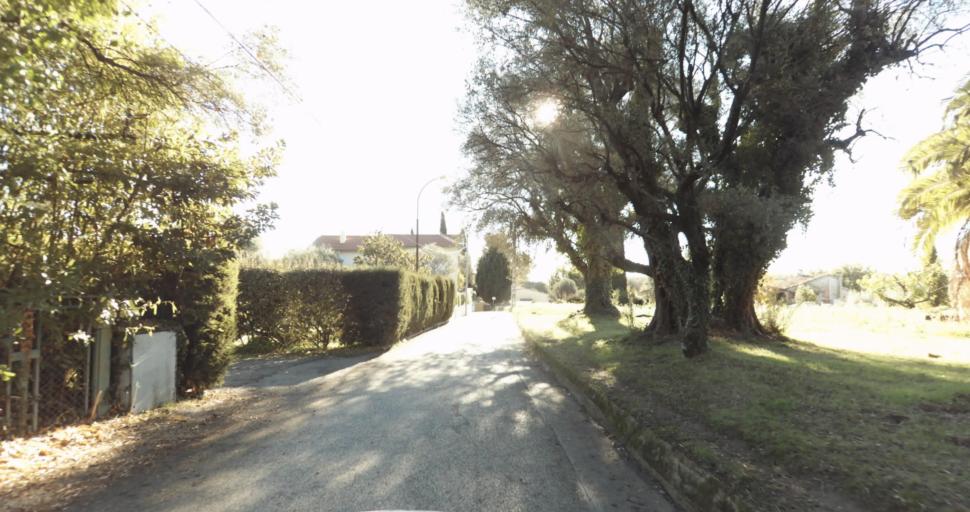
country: FR
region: Provence-Alpes-Cote d'Azur
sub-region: Departement des Alpes-Maritimes
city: Vence
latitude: 43.7211
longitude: 7.0896
